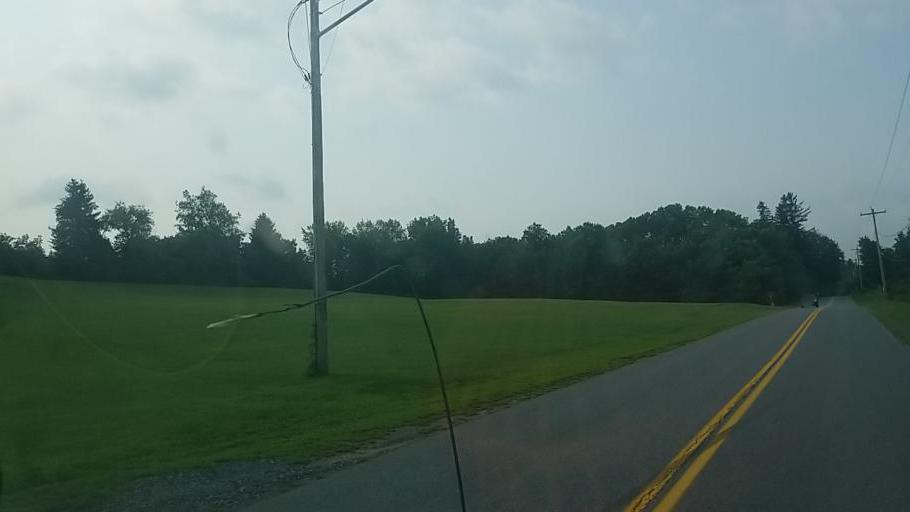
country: US
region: New York
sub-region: Fulton County
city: Johnstown
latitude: 43.0219
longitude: -74.3812
